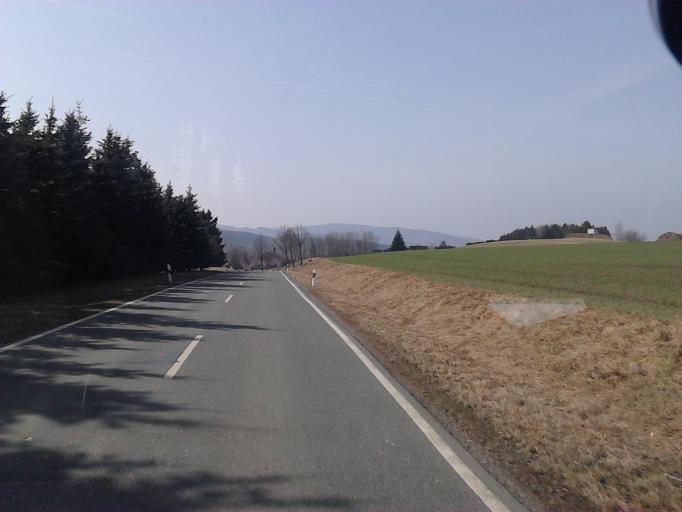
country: DE
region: Bavaria
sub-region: Upper Franconia
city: Presseck
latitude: 50.2746
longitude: 11.5615
